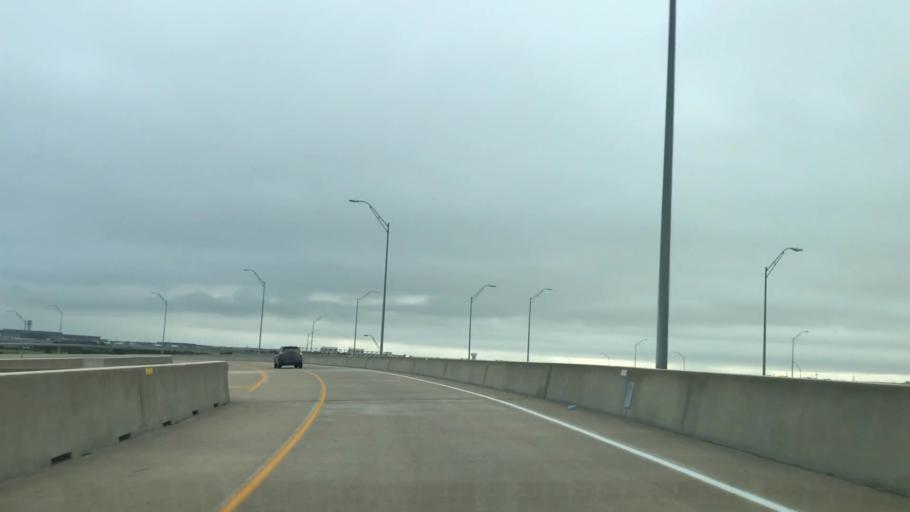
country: US
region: Texas
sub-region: Dallas County
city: Coppell
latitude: 32.9340
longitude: -97.0406
